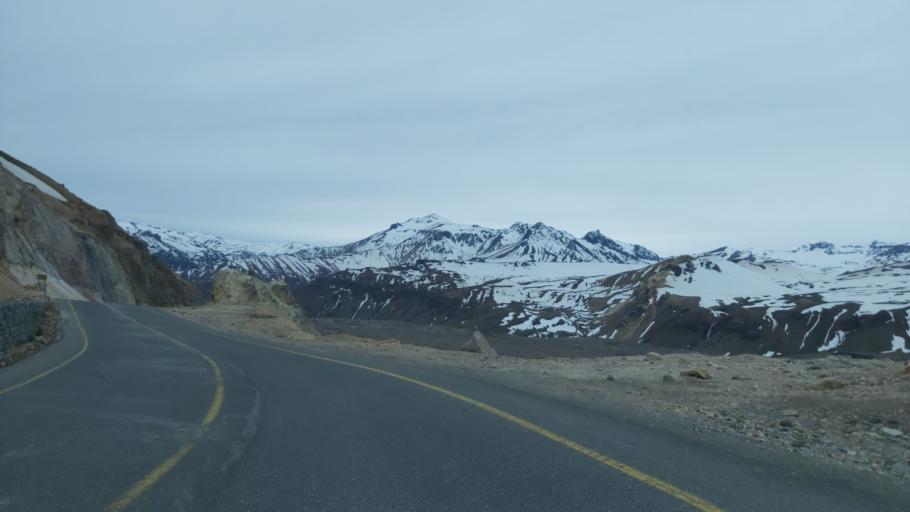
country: CL
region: Maule
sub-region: Provincia de Linares
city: Colbun
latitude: -35.9767
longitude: -70.5630
